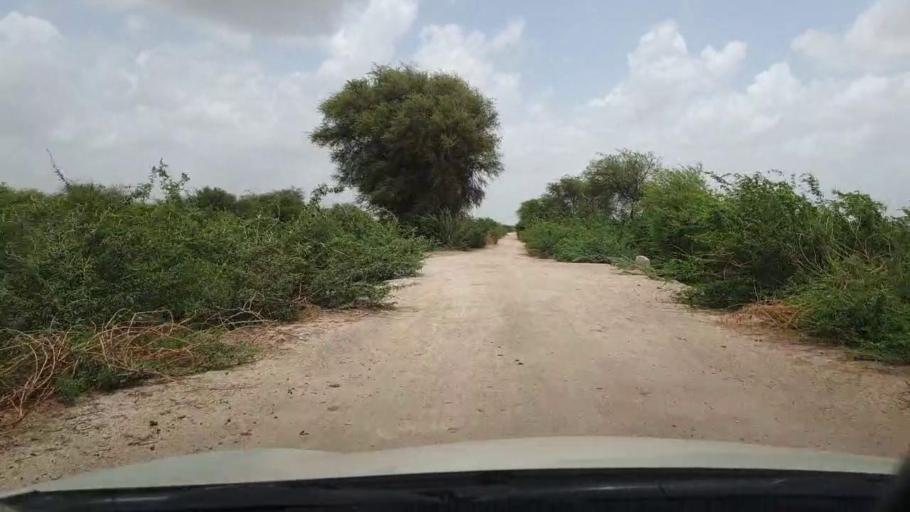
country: PK
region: Sindh
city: Kadhan
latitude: 24.3603
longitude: 68.9492
